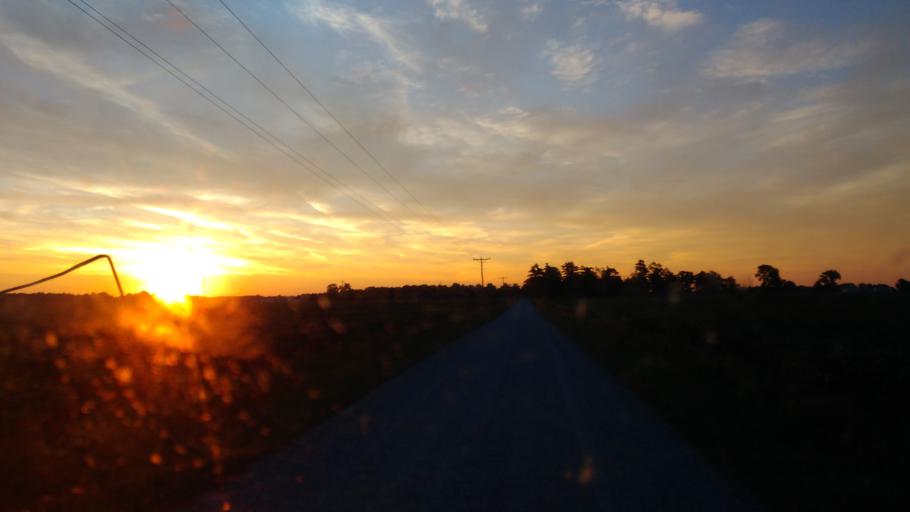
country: US
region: Indiana
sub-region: Wells County
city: Bluffton
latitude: 40.6845
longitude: -85.1140
